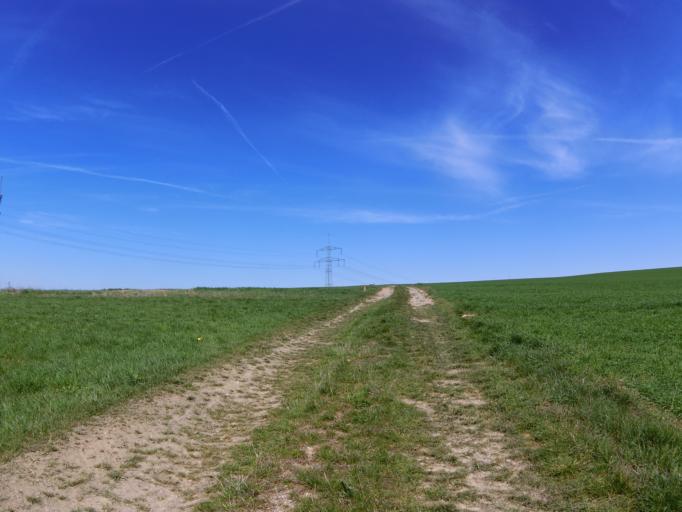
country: DE
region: Bavaria
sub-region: Regierungsbezirk Unterfranken
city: Rottendorf
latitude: 49.7846
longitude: 10.0534
